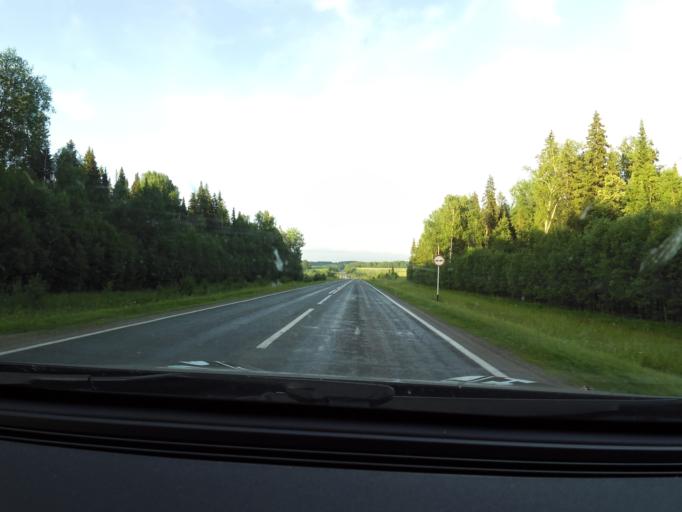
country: RU
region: Perm
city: Siva
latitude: 58.4880
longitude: 54.1693
